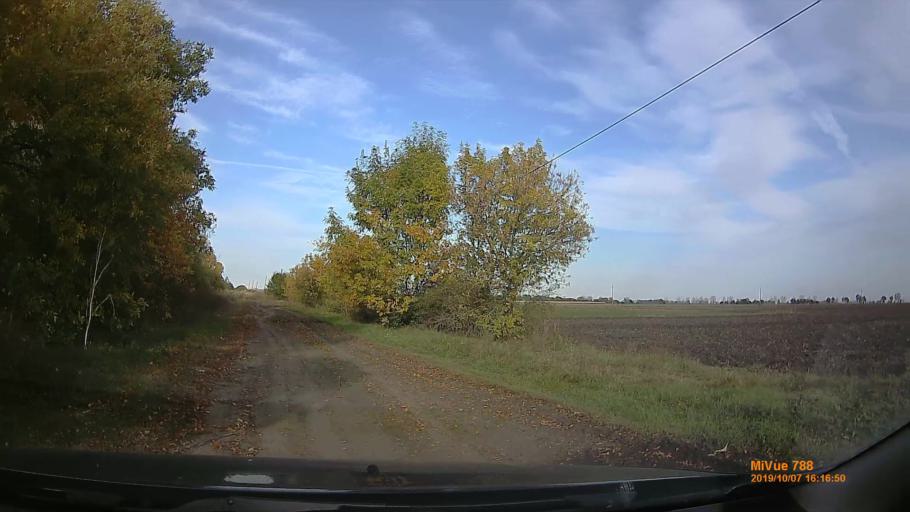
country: HU
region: Bekes
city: Szarvas
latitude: 46.8037
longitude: 20.6196
